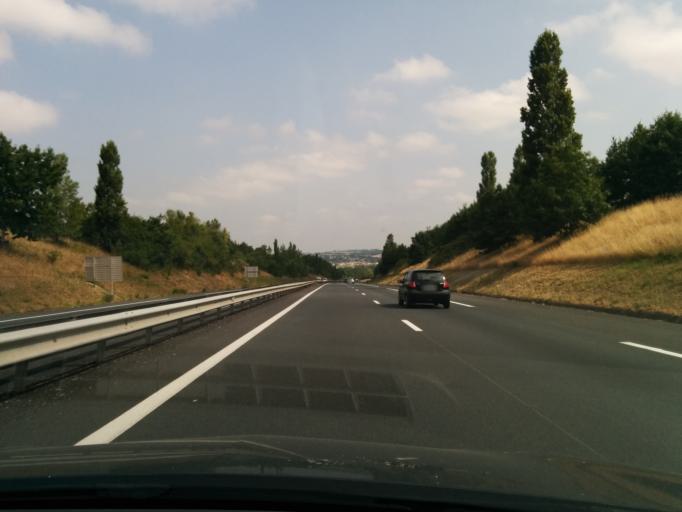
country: FR
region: Midi-Pyrenees
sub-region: Departement de la Haute-Garonne
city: Gragnague
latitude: 43.6781
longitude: 1.5608
